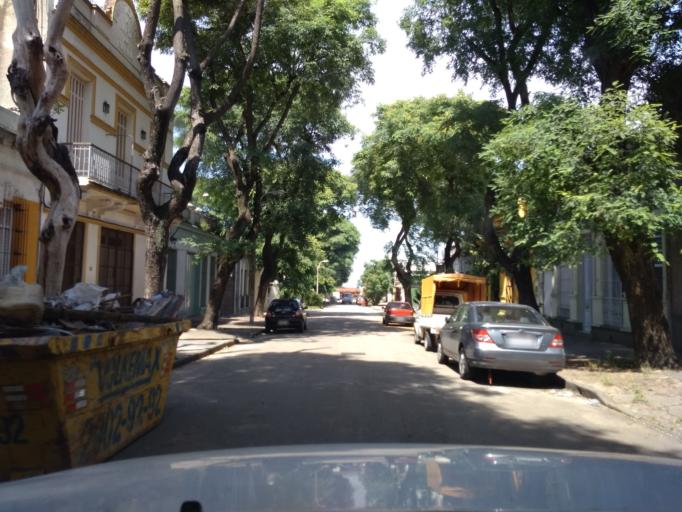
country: UY
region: Montevideo
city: Montevideo
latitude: -34.8777
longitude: -56.2008
